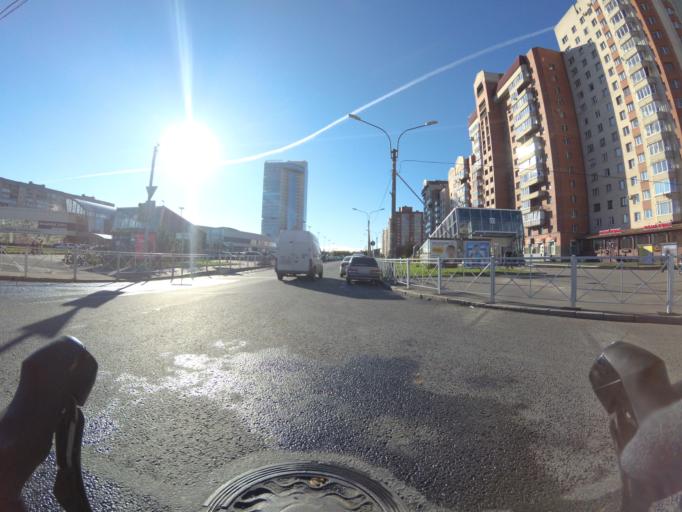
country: RU
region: Leningrad
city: Untolovo
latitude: 59.9886
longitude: 30.2027
